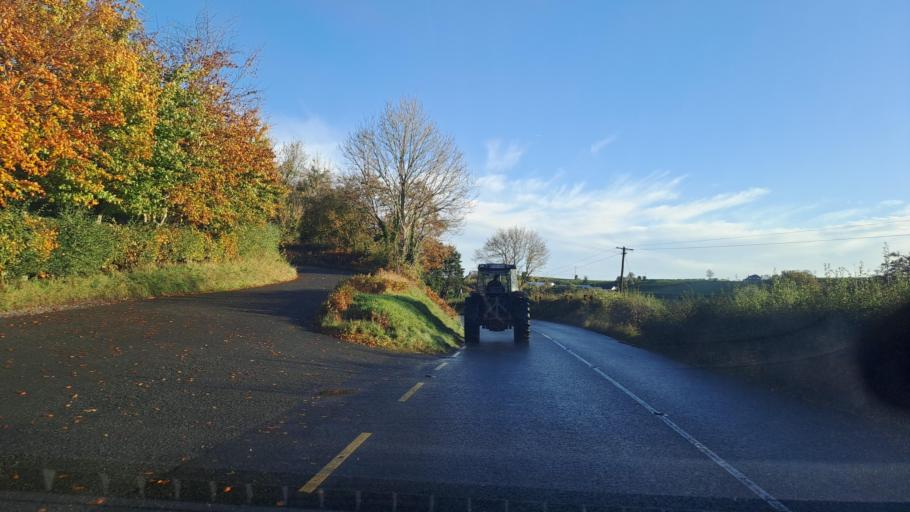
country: IE
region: Ulster
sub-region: County Monaghan
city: Monaghan
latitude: 54.2224
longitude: -6.9751
